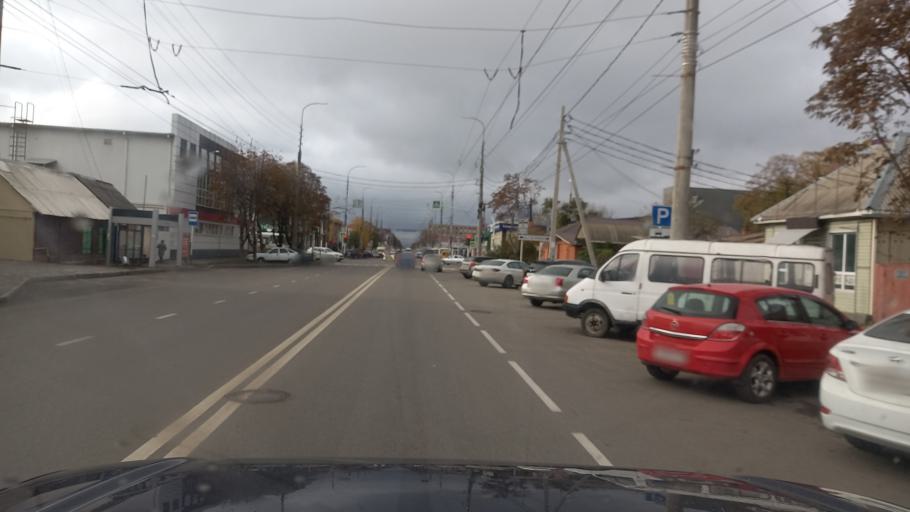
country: RU
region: Adygeya
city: Maykop
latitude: 44.6084
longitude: 40.1133
